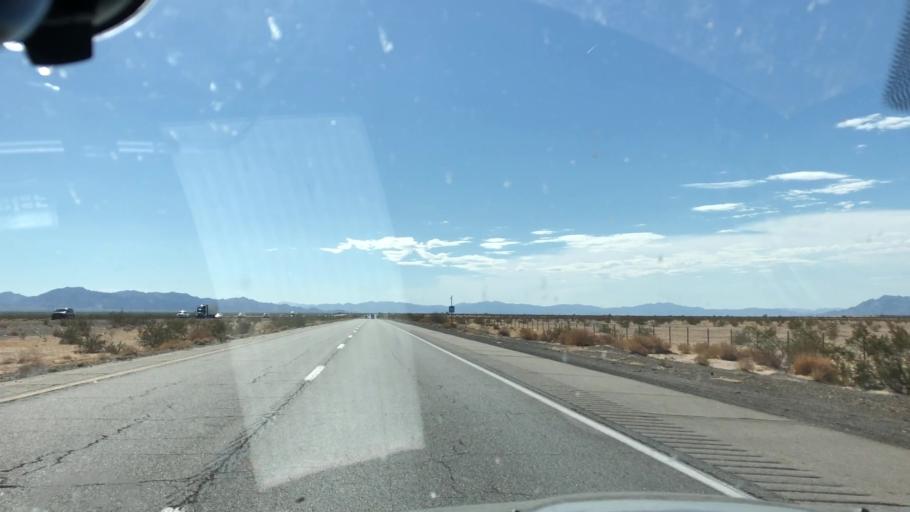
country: US
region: California
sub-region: Riverside County
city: Mesa Verde
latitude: 33.6412
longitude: -115.1015
